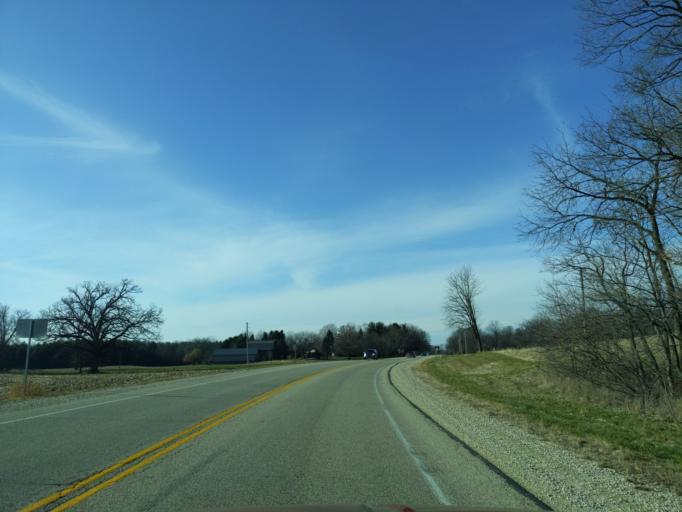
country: US
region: Wisconsin
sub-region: Rock County
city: Milton
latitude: 42.8227
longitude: -88.9541
